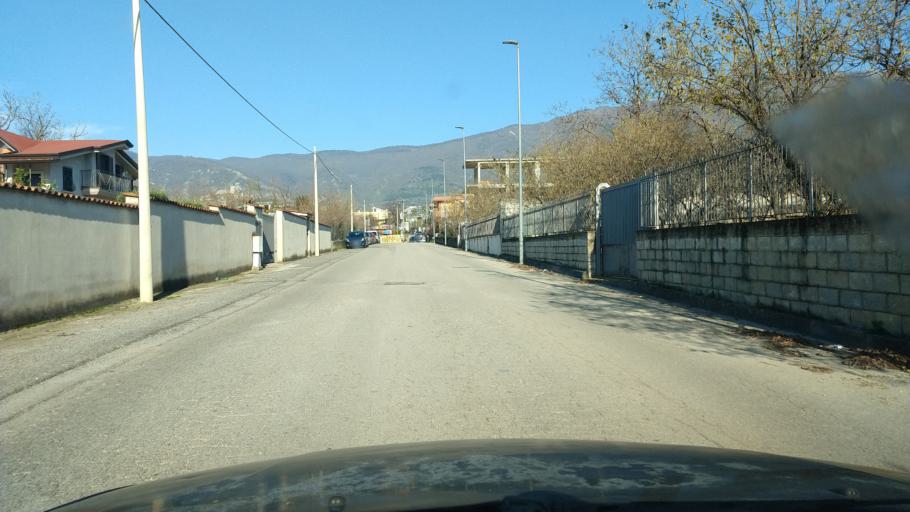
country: IT
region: Campania
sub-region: Provincia di Avellino
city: Sperone
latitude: 40.9512
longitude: 14.5984
